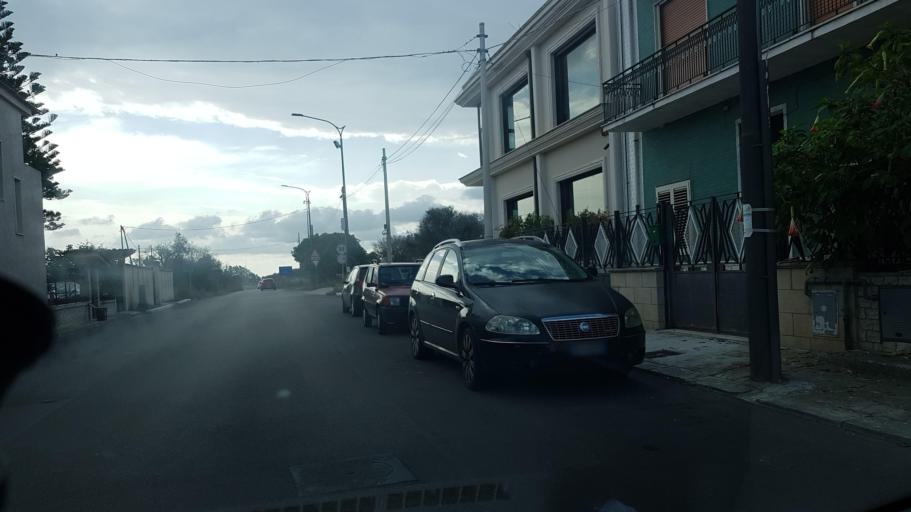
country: IT
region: Apulia
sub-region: Provincia di Brindisi
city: San Pietro Vernotico
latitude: 40.4785
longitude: 18.0066
